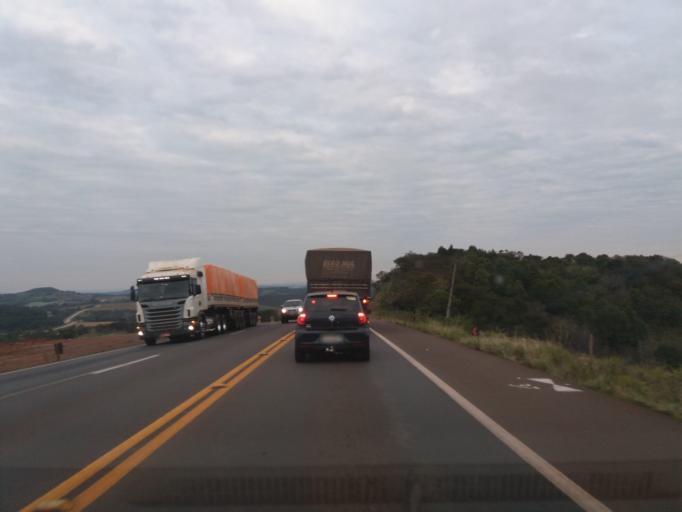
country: BR
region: Parana
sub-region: Cascavel
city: Cascavel
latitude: -25.1946
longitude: -53.6024
